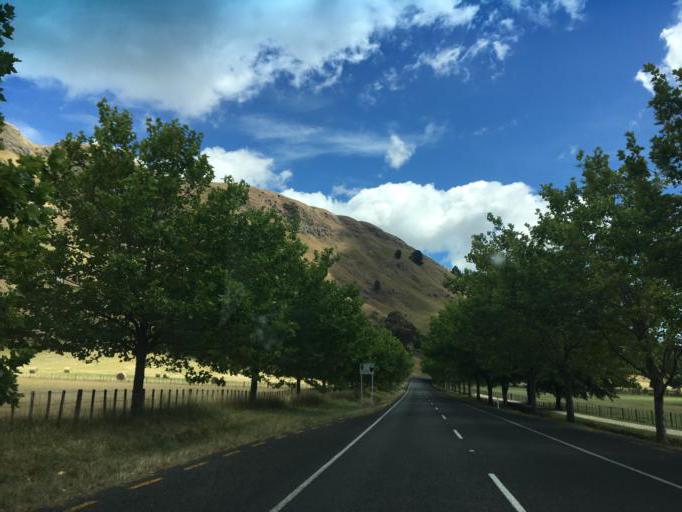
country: NZ
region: Hawke's Bay
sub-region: Hastings District
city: Hastings
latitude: -39.6924
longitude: 176.9205
